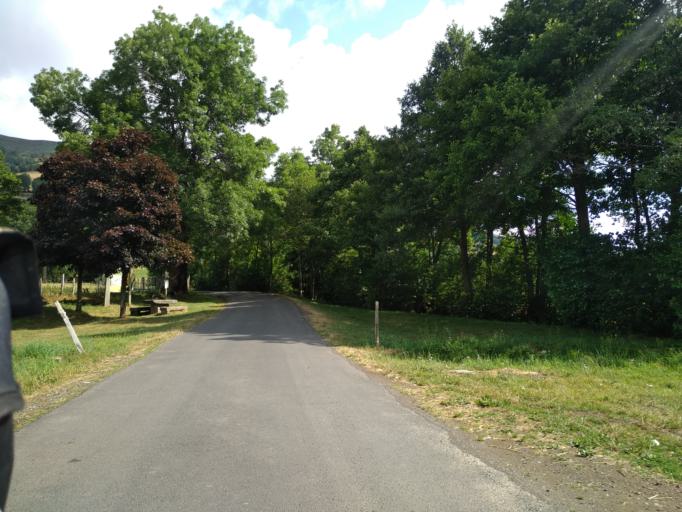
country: FR
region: Auvergne
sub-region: Departement du Cantal
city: Murat
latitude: 45.1335
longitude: 2.7454
